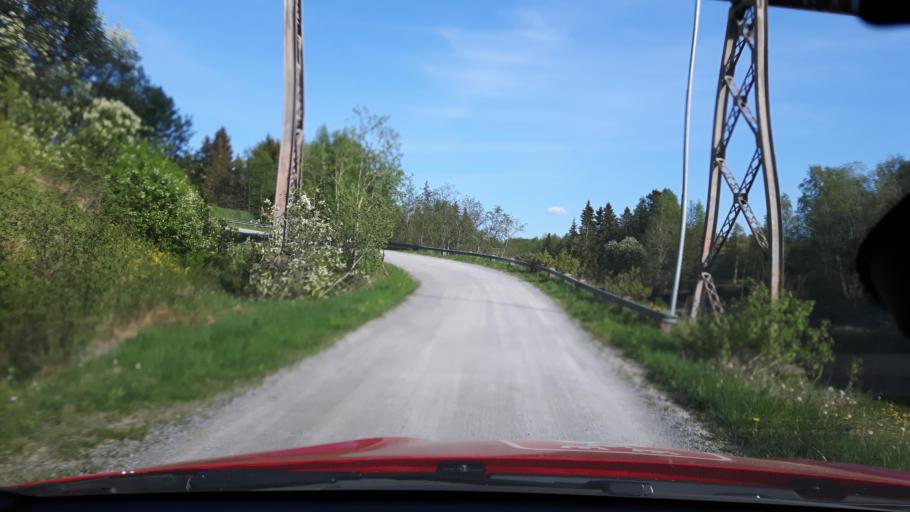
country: SE
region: Jaemtland
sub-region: Bergs Kommun
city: Hoverberg
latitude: 62.9152
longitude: 14.5201
